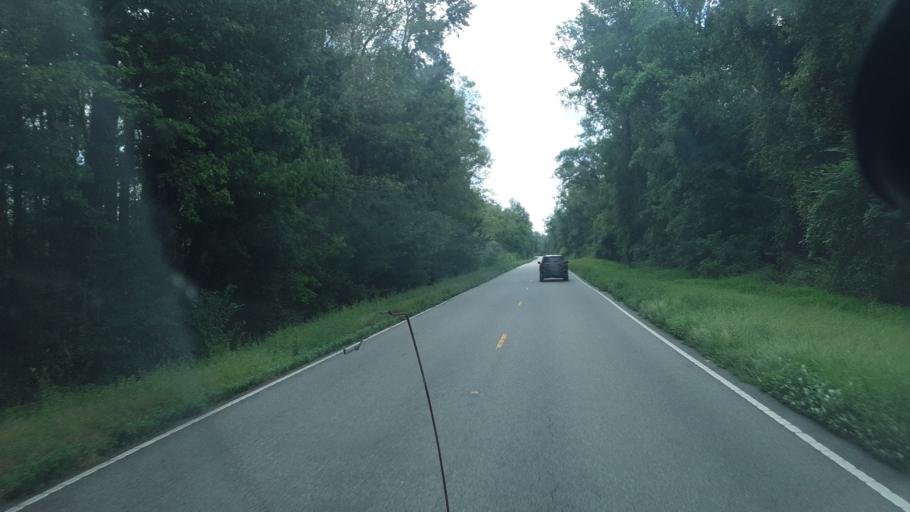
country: US
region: North Carolina
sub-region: Robeson County
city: Fairmont
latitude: 34.3507
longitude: -79.0815
